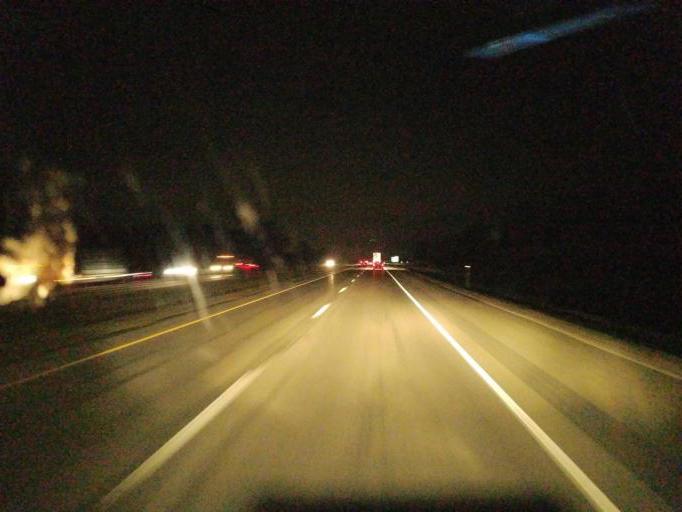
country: US
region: Iowa
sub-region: Dallas County
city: De Soto
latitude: 41.5434
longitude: -93.9823
